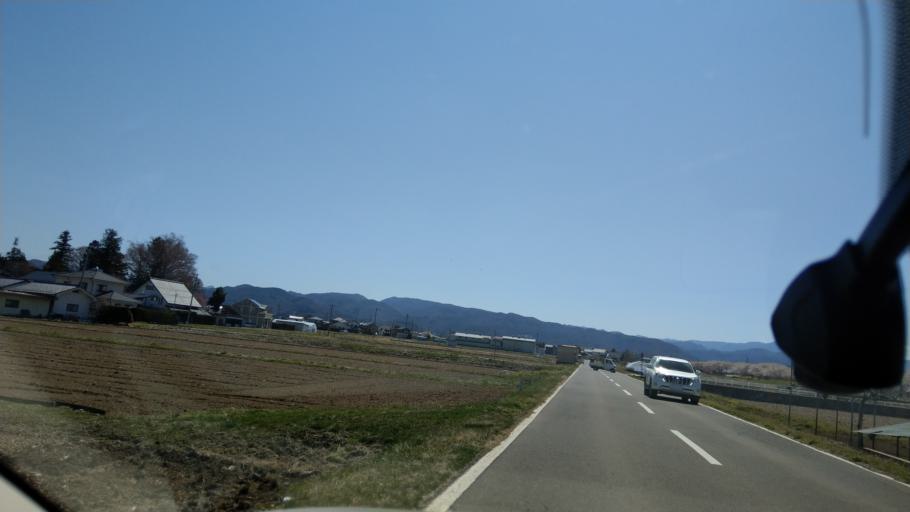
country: JP
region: Nagano
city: Saku
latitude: 36.2399
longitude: 138.4643
